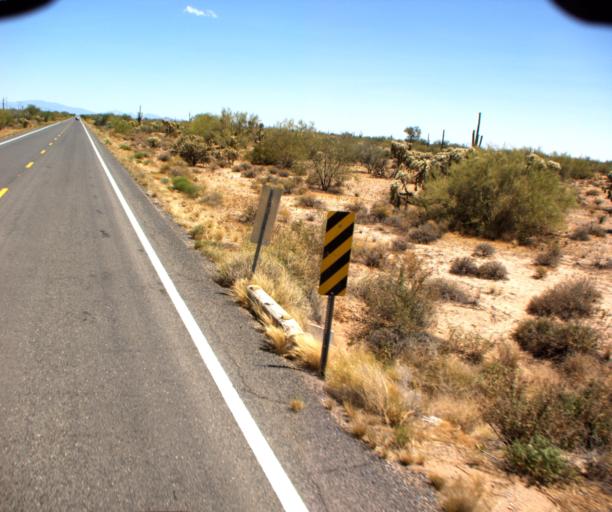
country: US
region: Arizona
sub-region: Pinal County
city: Florence
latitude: 32.8840
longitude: -111.2627
